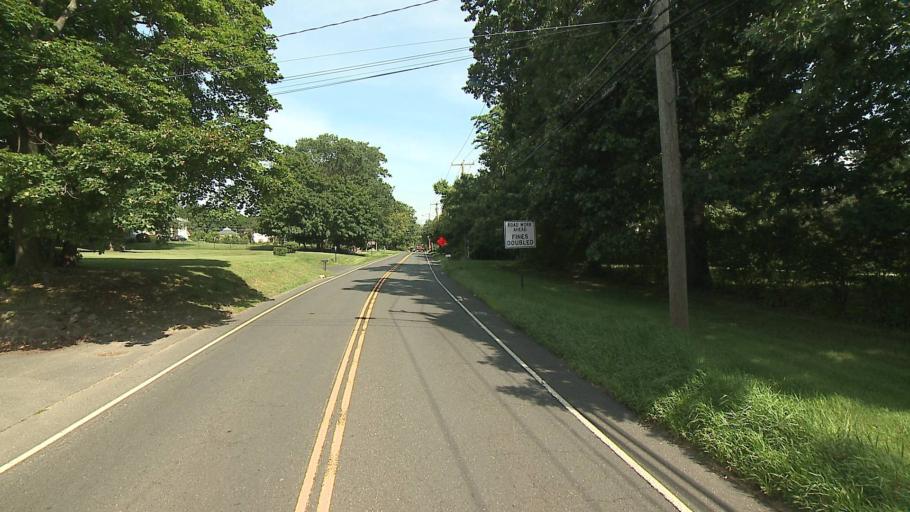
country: US
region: Connecticut
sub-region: Fairfield County
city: Danbury
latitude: 41.4104
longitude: -73.4690
